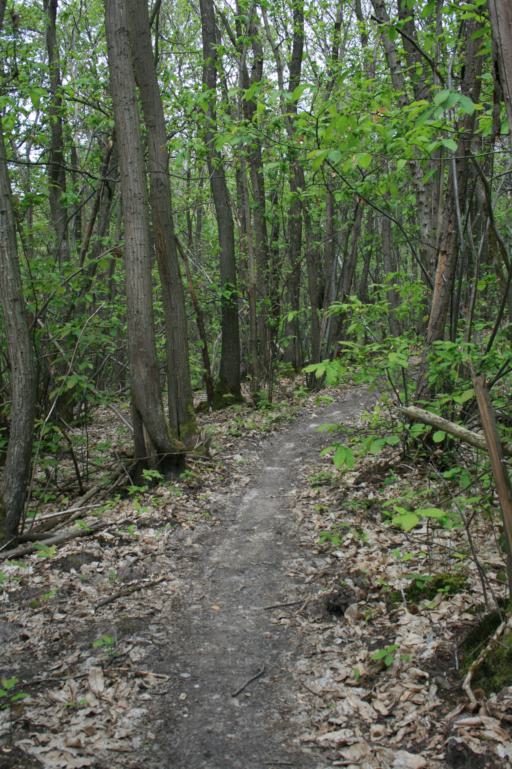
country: FR
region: Ile-de-France
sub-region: Departement des Yvelines
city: Vaux-sur-Seine
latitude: 49.0063
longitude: 1.9911
